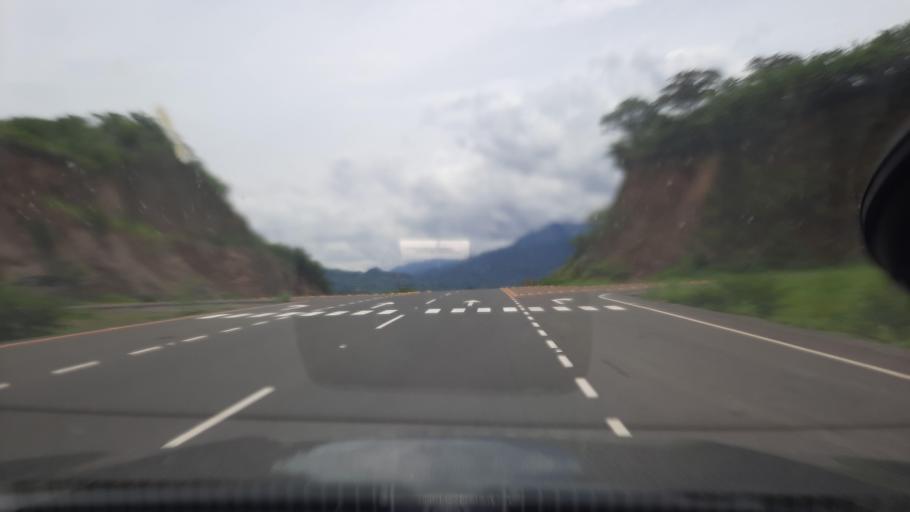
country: HN
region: Valle
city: Aramecina
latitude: 13.7462
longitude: -87.7171
